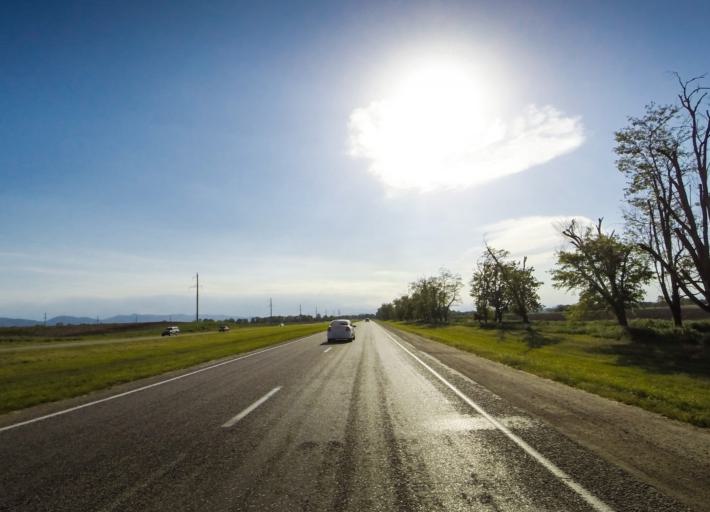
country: RU
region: Kabardino-Balkariya
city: Urvan'
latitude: 43.5036
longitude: 43.7307
